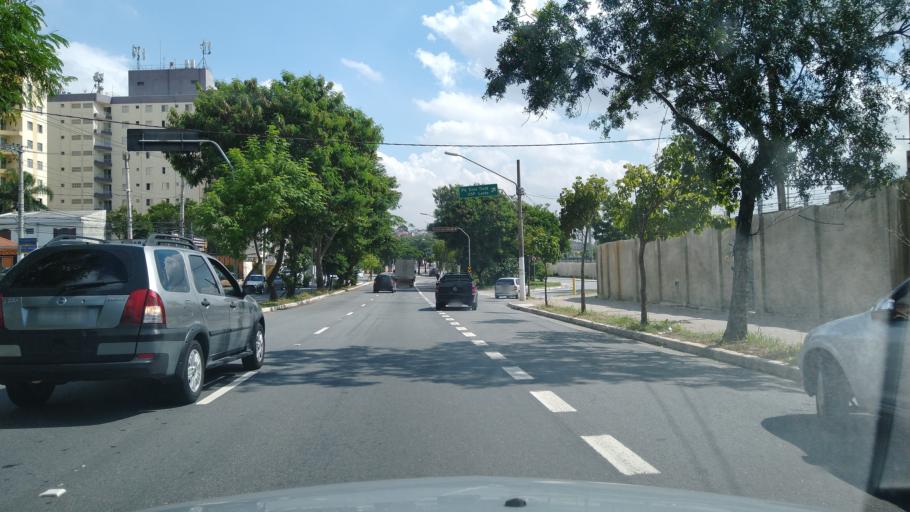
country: BR
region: Sao Paulo
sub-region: Guarulhos
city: Guarulhos
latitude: -23.4992
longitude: -46.5219
